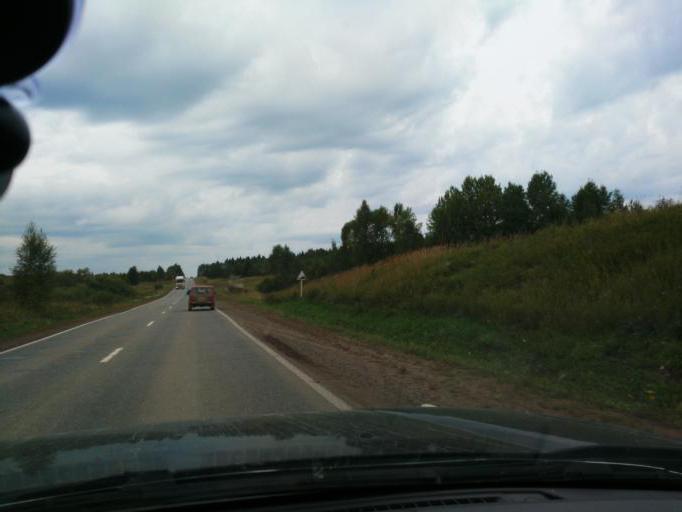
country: RU
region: Perm
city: Chernushka
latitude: 56.7502
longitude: 56.1531
